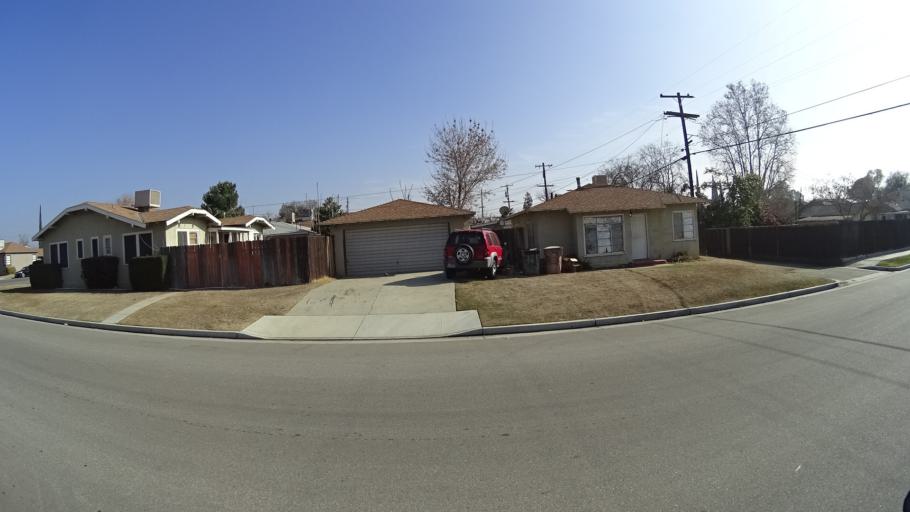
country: US
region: California
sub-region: Kern County
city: Bakersfield
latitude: 35.3883
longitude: -118.9905
